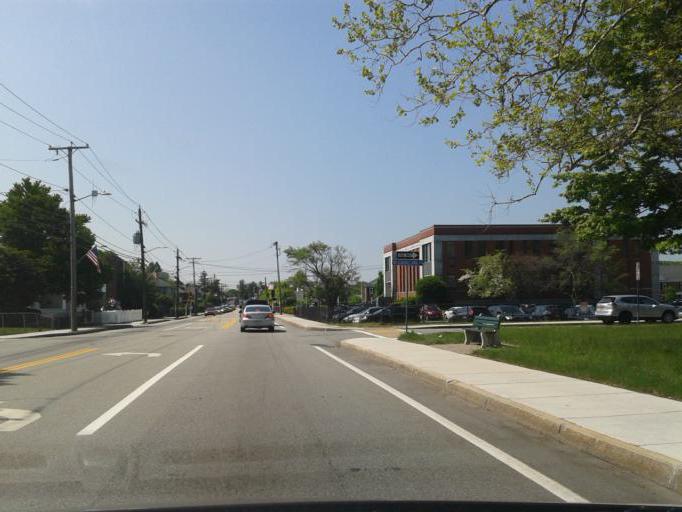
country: US
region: Massachusetts
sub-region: Middlesex County
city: Framingham
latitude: 42.2943
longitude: -71.4090
